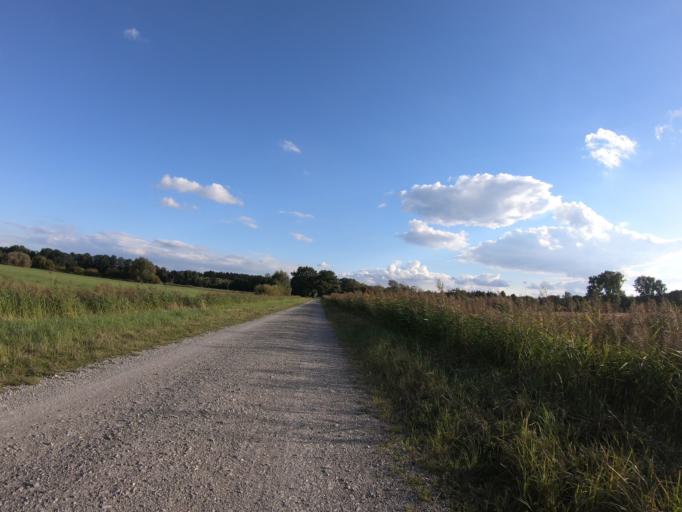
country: DE
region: Lower Saxony
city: Osloss
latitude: 52.4280
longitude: 10.6744
